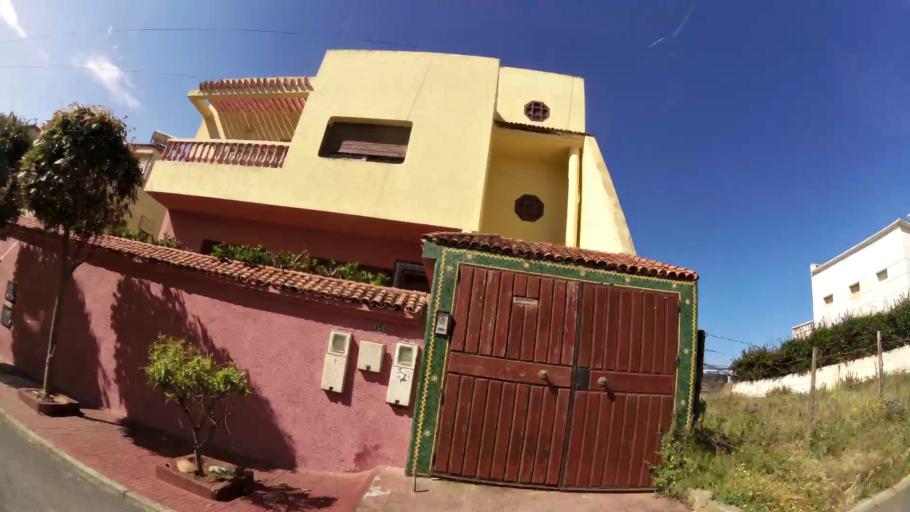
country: MA
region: Rabat-Sale-Zemmour-Zaer
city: Sale
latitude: 34.0682
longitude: -6.8042
